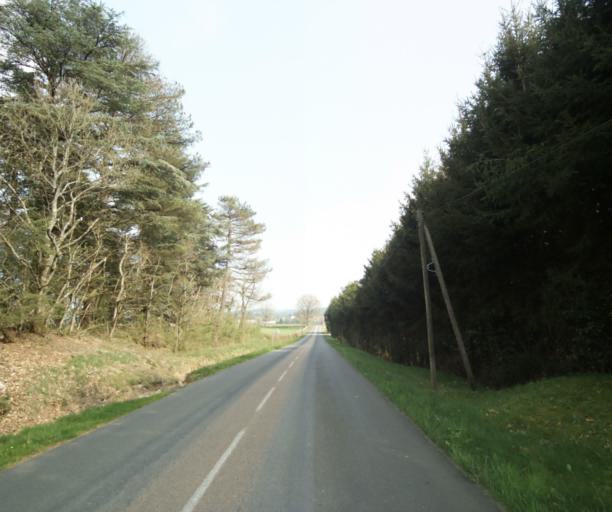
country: FR
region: Bourgogne
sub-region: Departement de Saone-et-Loire
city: Charolles
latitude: 46.4899
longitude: 4.4300
